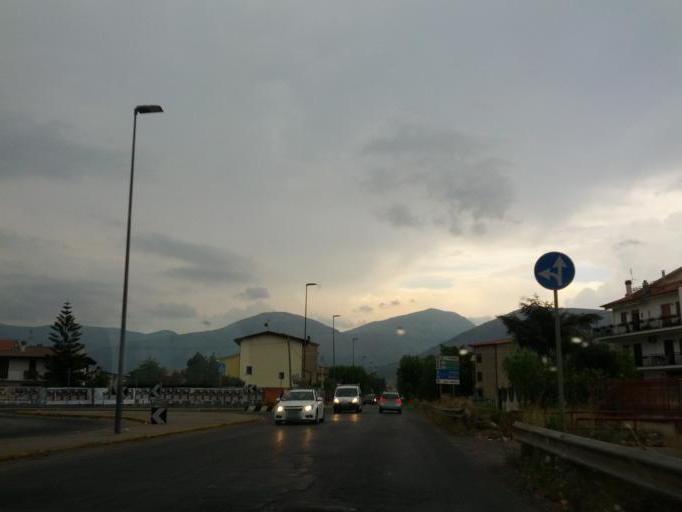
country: IT
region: Latium
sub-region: Provincia di Latina
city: Fondi
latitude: 41.3398
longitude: 13.4277
